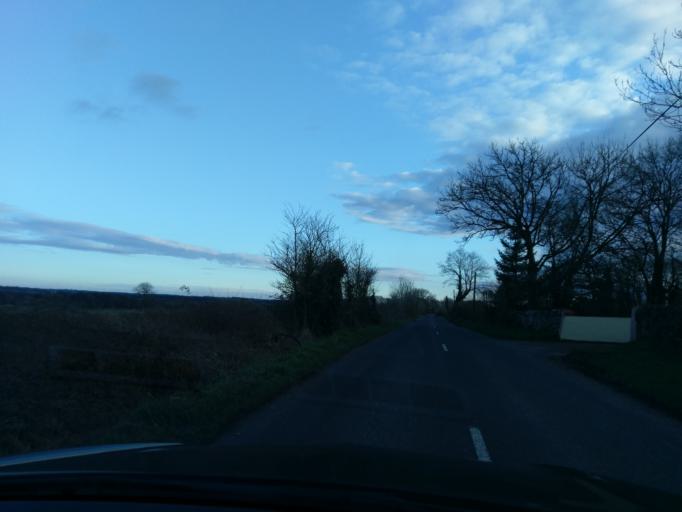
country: IE
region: Connaught
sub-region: County Galway
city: Athenry
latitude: 53.4234
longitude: -8.6904
